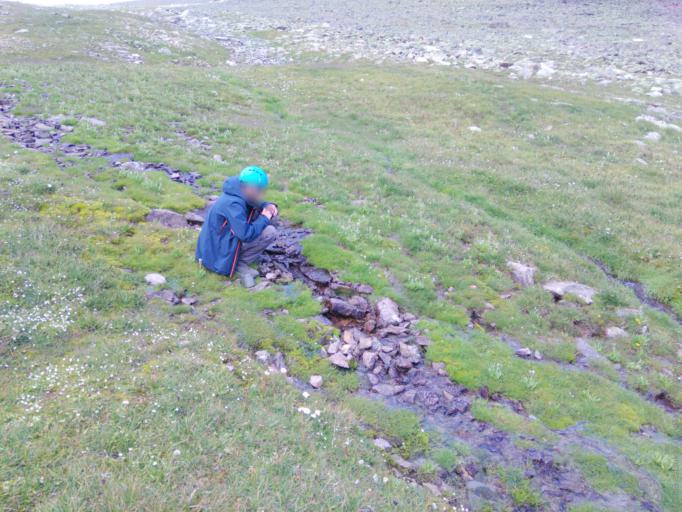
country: RU
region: Kabardino-Balkariya
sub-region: El'brusskiy Rayon
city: El'brus
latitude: 43.3312
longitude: 42.6675
